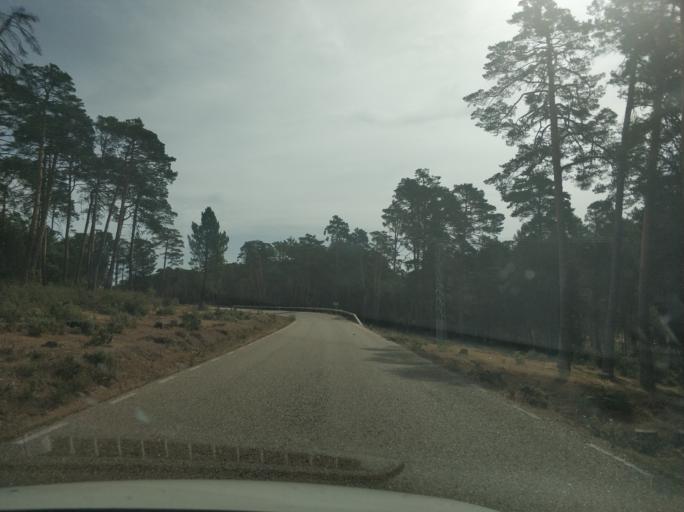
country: ES
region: Castille and Leon
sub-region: Provincia de Soria
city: Navaleno
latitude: 41.8534
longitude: -2.9624
